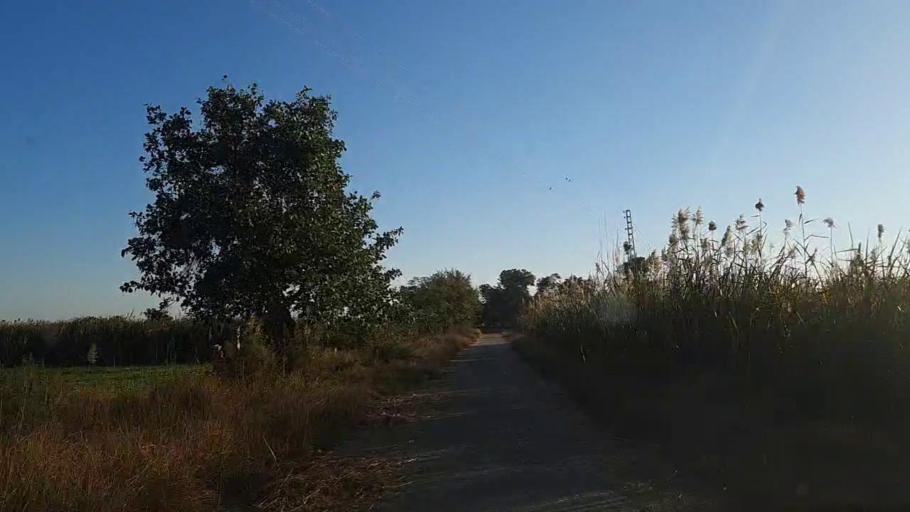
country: PK
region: Sindh
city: Sanghar
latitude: 26.1391
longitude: 68.9436
